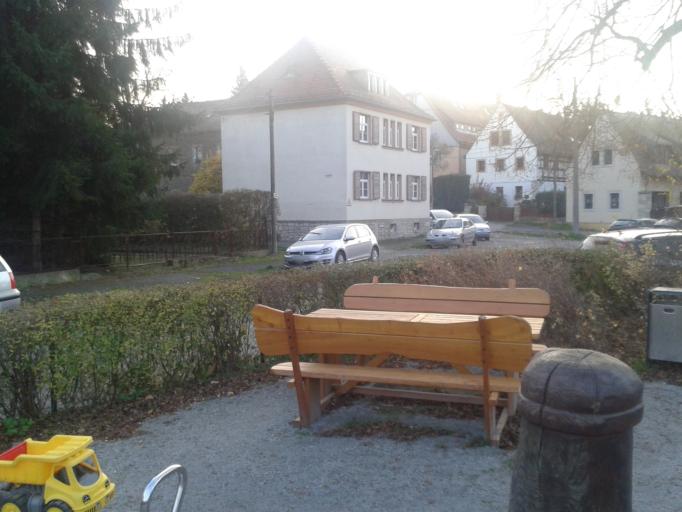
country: DE
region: Saxony
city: Bannewitz
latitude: 51.0150
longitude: 13.7410
